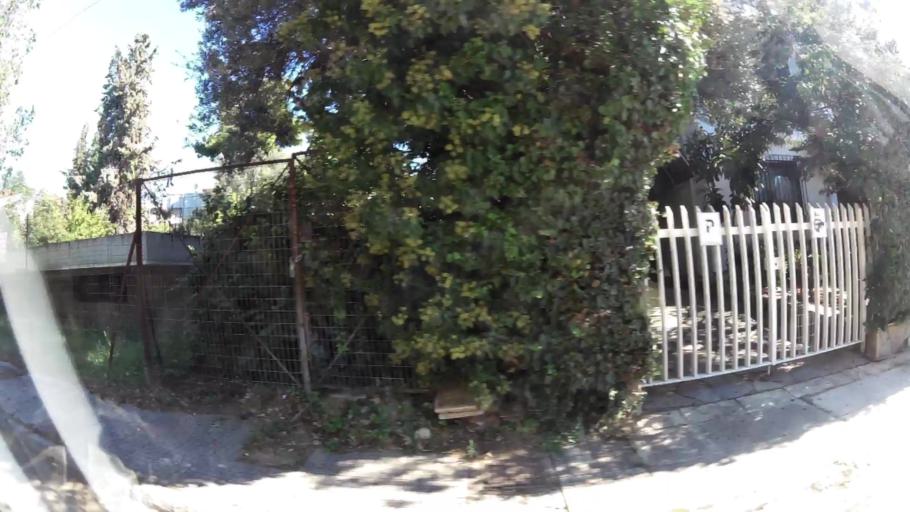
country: GR
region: Attica
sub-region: Nomarchia Athinas
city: Kifisia
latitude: 38.0846
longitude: 23.8003
